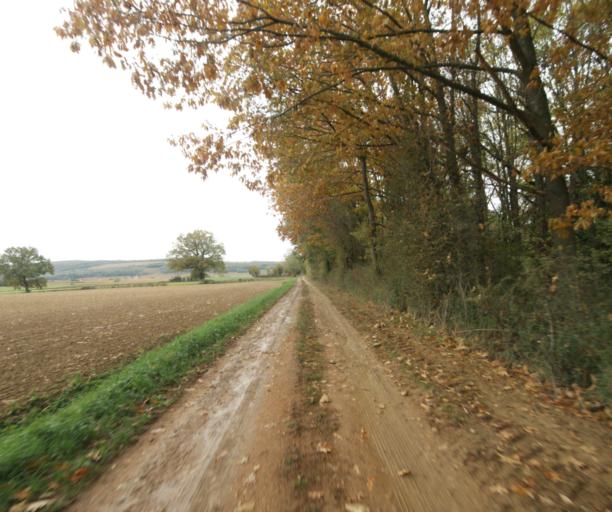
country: FR
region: Rhone-Alpes
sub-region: Departement de l'Ain
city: Pont-de-Vaux
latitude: 46.4615
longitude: 4.8737
